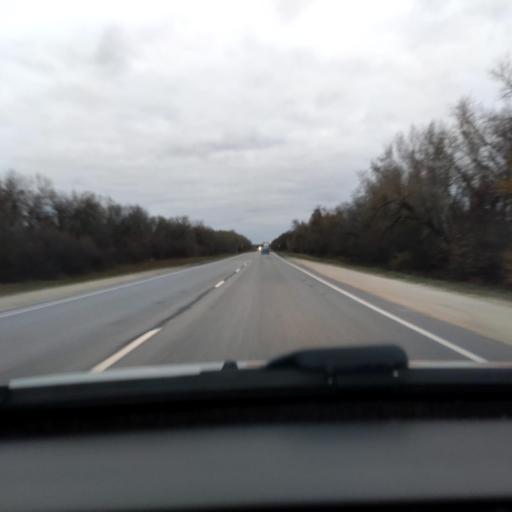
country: RU
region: Lipetsk
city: Borinskoye
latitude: 52.4108
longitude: 39.2466
